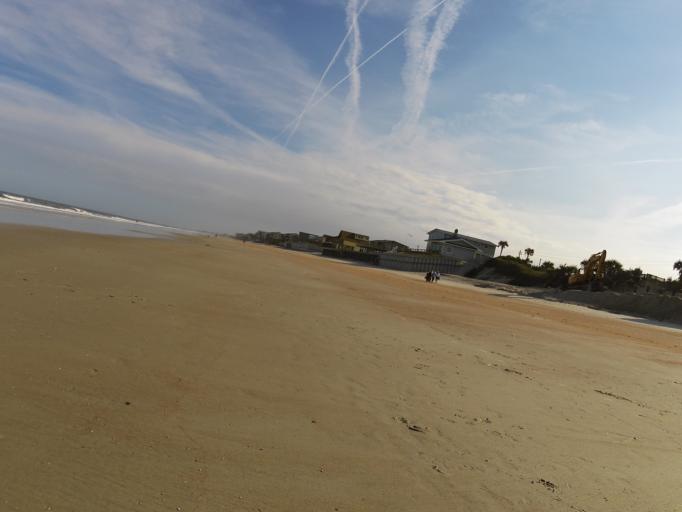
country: US
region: Florida
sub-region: Saint Johns County
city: Villano Beach
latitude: 29.9513
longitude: -81.3028
